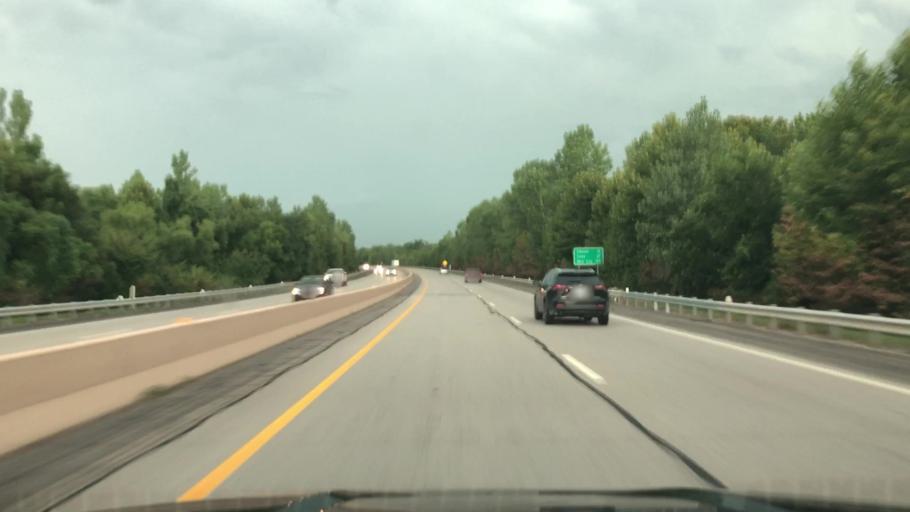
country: US
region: Oklahoma
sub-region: Rogers County
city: Claremore
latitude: 36.2944
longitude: -95.6062
